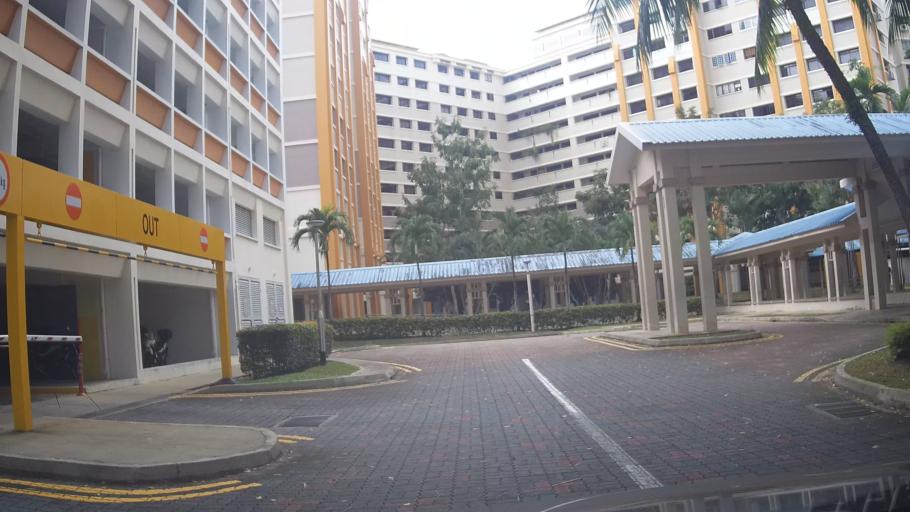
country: MY
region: Johor
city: Johor Bahru
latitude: 1.4450
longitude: 103.7998
